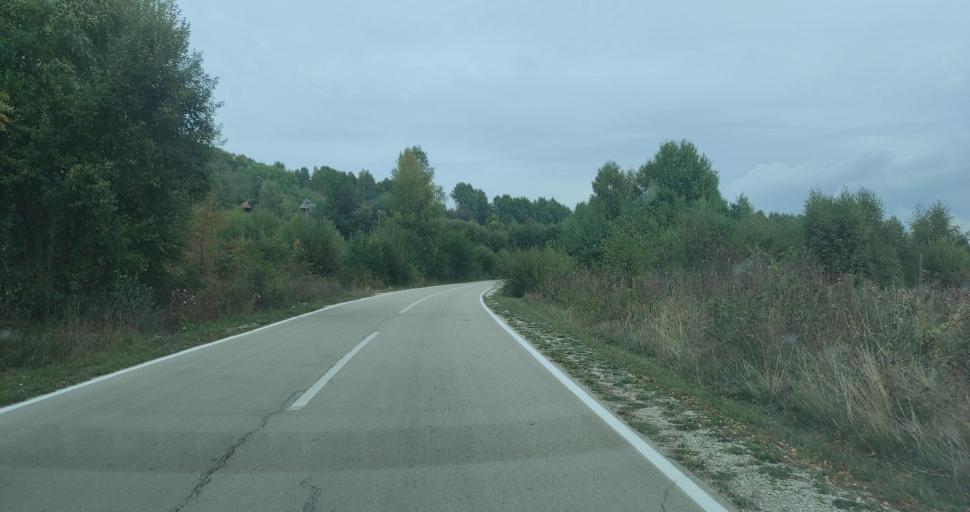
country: RS
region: Central Serbia
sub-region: Jablanicki Okrug
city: Crna Trava
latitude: 42.7107
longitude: 22.3276
